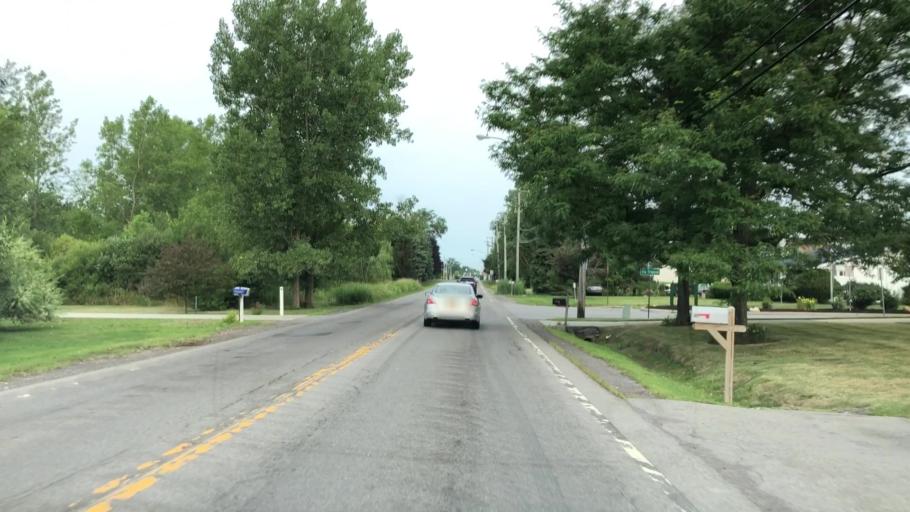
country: US
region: New York
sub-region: Erie County
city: Depew
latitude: 42.8804
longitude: -78.6894
